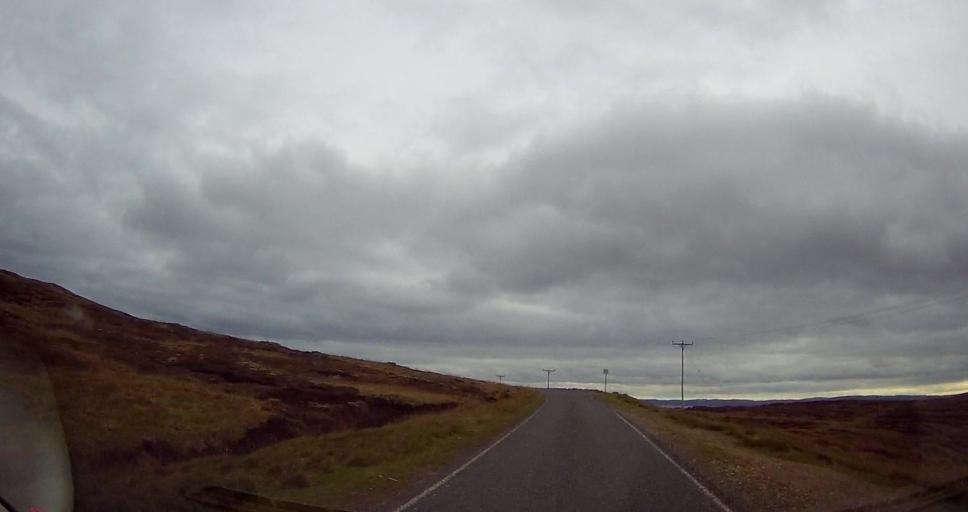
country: GB
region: Scotland
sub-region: Shetland Islands
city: Shetland
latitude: 60.5183
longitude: -1.0581
